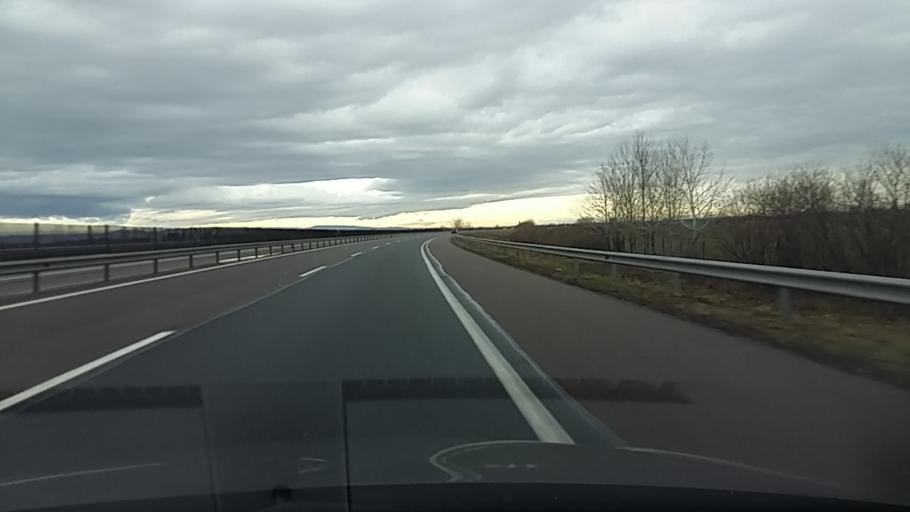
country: HU
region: Heves
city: Fuzesabony
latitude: 47.7468
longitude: 20.4473
